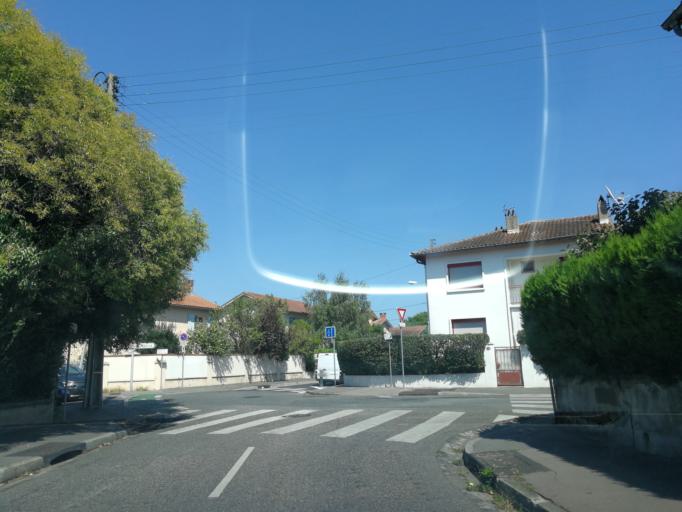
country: FR
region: Midi-Pyrenees
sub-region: Departement de la Haute-Garonne
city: L'Union
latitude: 43.6293
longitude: 1.4716
